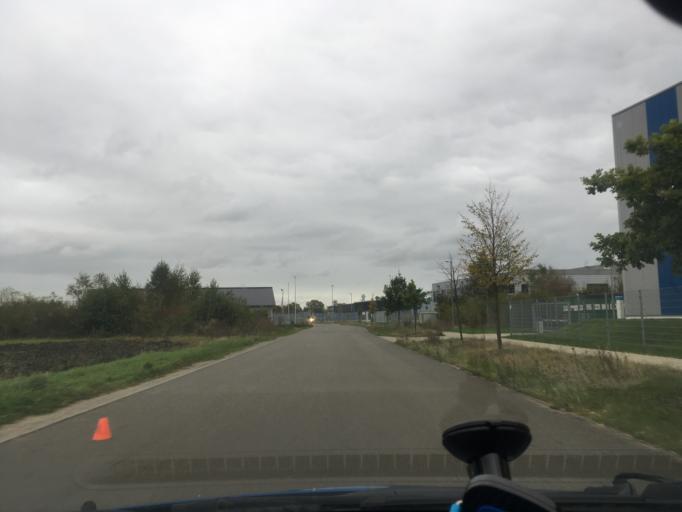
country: DE
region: Lower Saxony
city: Wittorf
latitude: 53.3151
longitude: 10.3687
